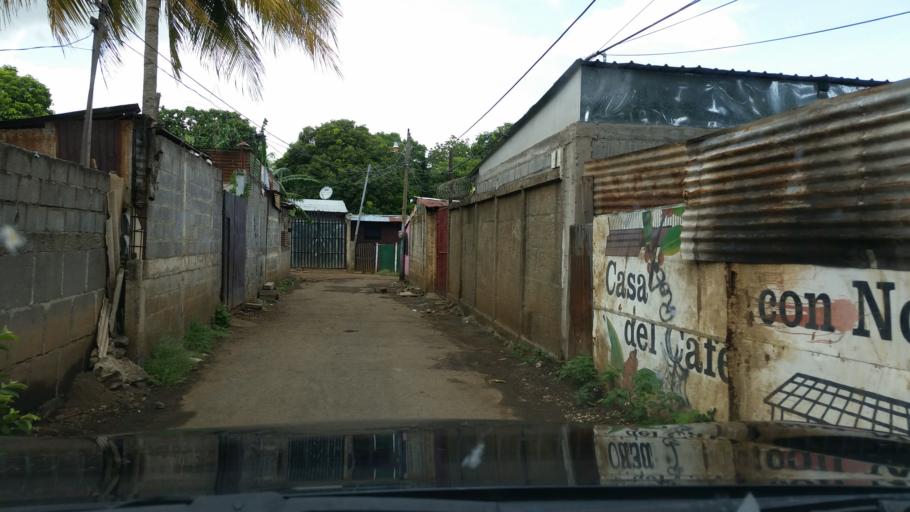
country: NI
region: Managua
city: Managua
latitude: 12.1288
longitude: -86.2764
